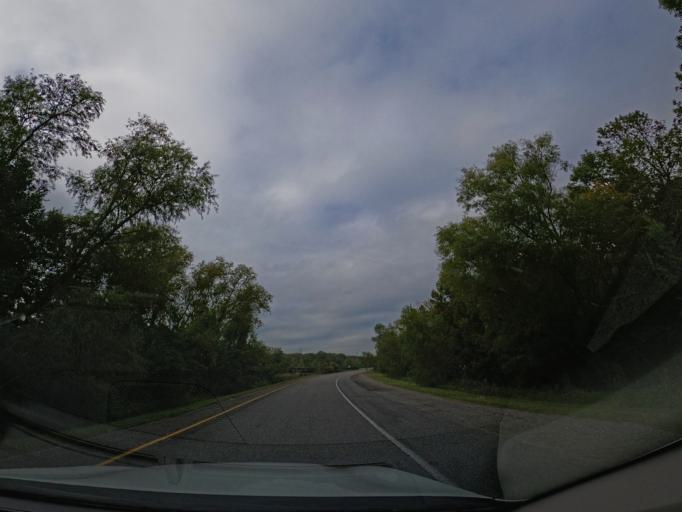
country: US
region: Louisiana
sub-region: Saint Mary Parish
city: Amelia
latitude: 29.6686
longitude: -91.0459
